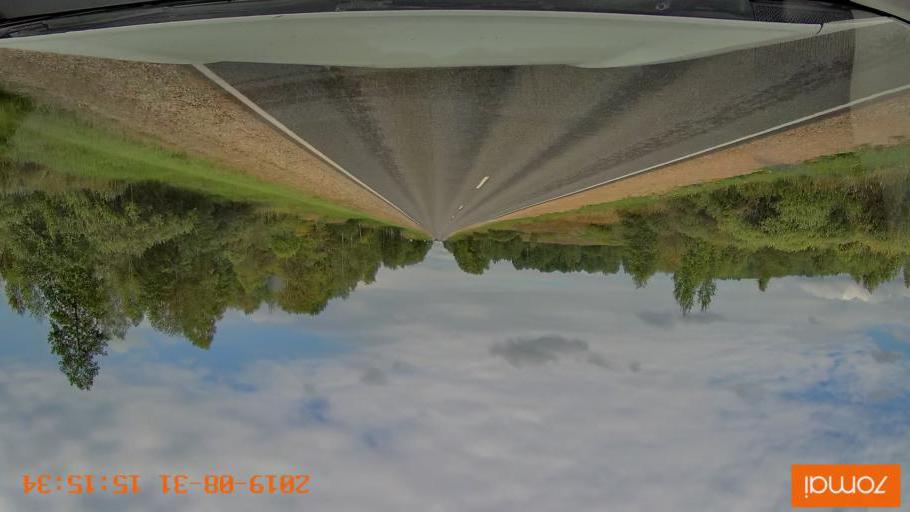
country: RU
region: Kaluga
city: Baryatino
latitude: 54.4526
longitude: 34.3295
